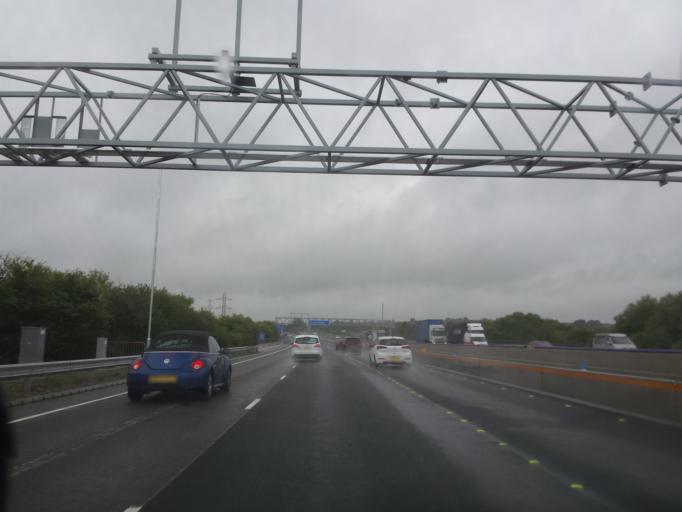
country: GB
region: England
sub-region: Derbyshire
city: Staveley
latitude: 53.2544
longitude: -1.3235
